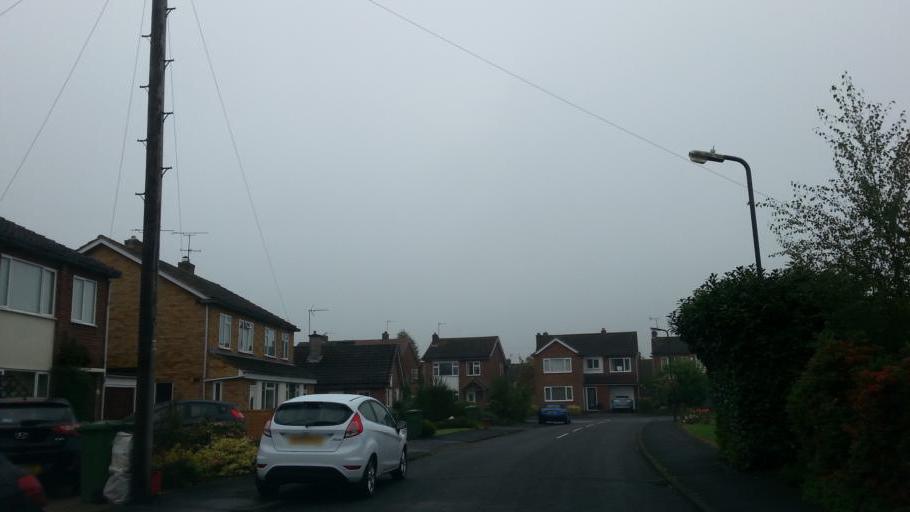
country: GB
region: England
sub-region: Warwickshire
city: Kenilworth
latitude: 52.3525
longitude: -1.5906
